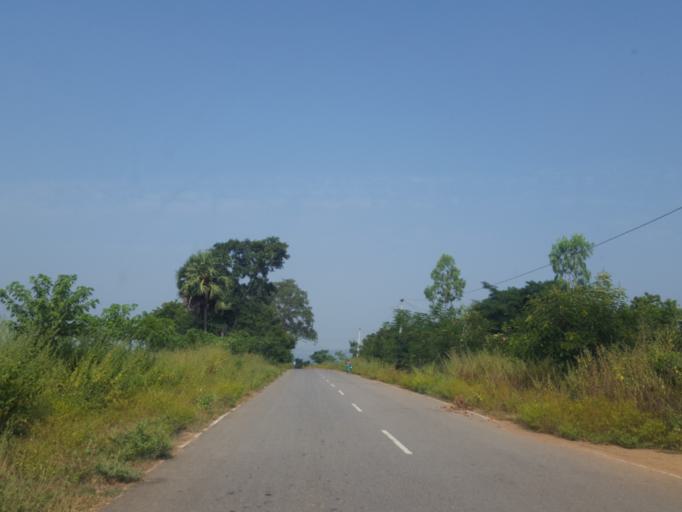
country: IN
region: Telangana
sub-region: Khammam
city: Yellandu
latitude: 17.6476
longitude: 80.2912
